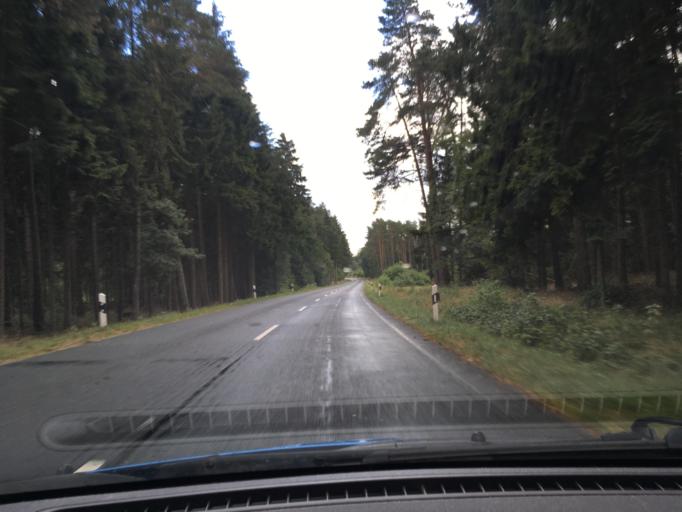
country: DE
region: Lower Saxony
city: Wietzendorf
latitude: 52.9194
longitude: 10.0133
